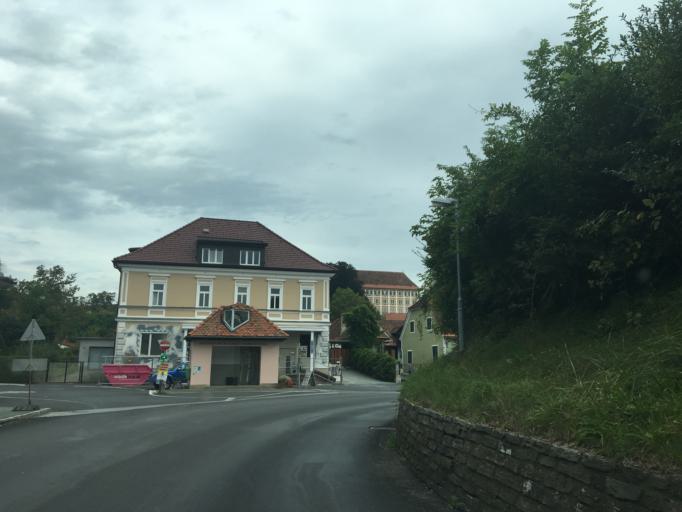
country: AT
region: Styria
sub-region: Politischer Bezirk Deutschlandsberg
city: Stainz
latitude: 46.8932
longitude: 15.2619
